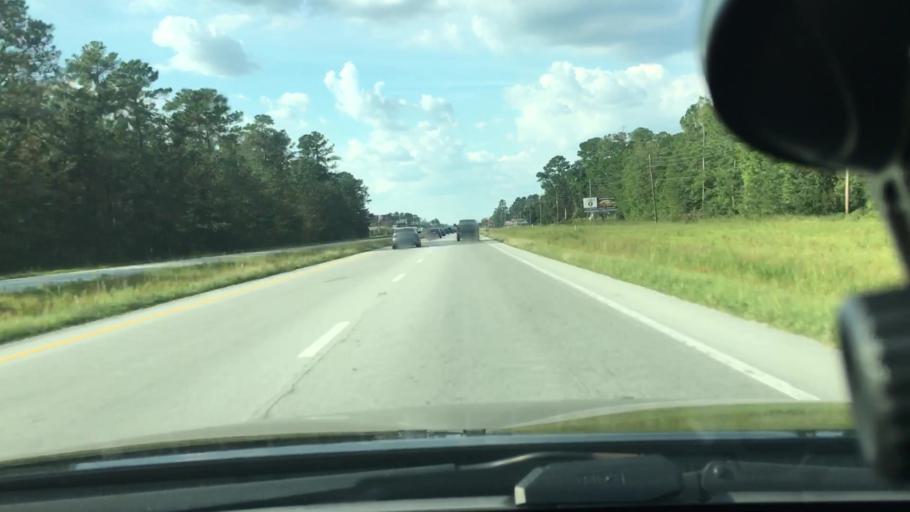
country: US
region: North Carolina
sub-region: Craven County
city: James City
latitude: 35.0529
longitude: -77.0157
